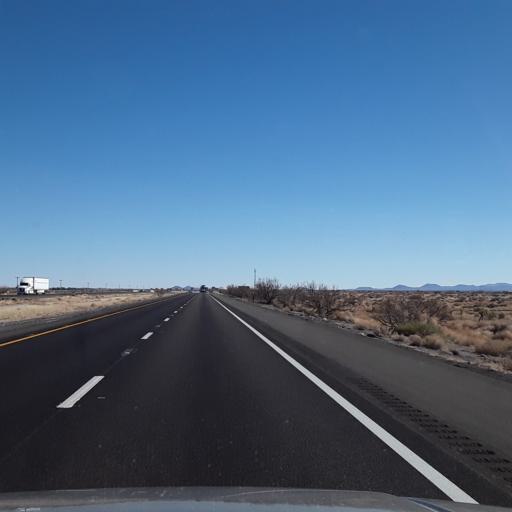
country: US
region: New Mexico
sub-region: Luna County
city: Deming
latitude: 32.2477
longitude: -107.4599
